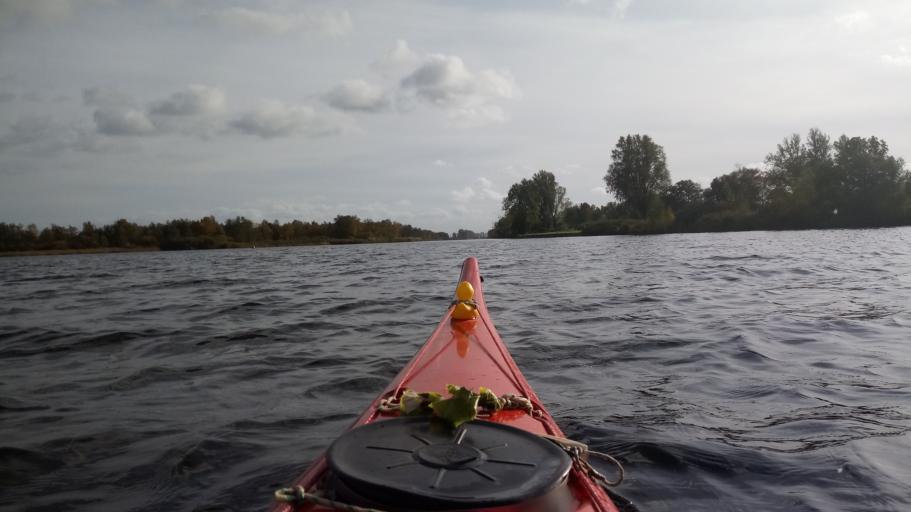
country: NL
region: Overijssel
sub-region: Gemeente Steenwijkerland
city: Wanneperveen
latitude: 52.6810
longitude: 6.0891
